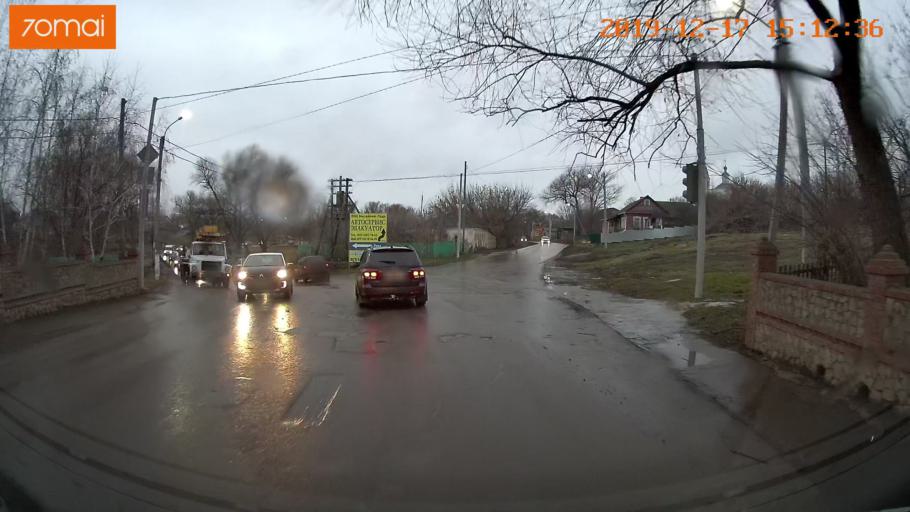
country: RU
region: Rjazan
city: Mikhaylov
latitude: 54.2343
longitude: 39.0249
